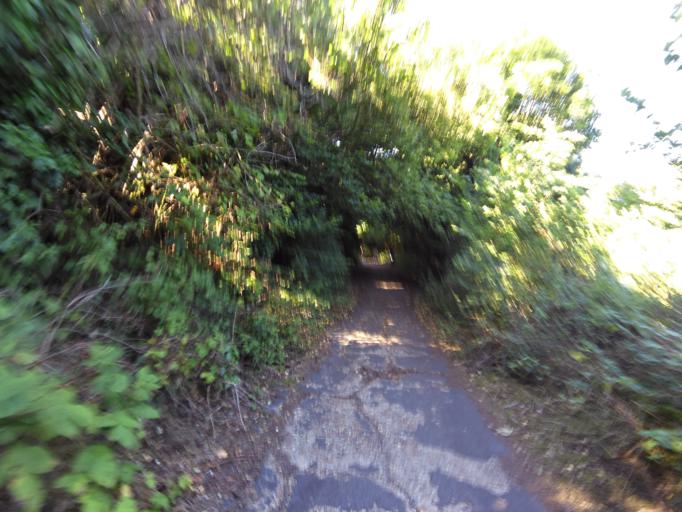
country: GB
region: England
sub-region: Suffolk
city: Kesgrave
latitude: 52.0651
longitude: 1.2652
